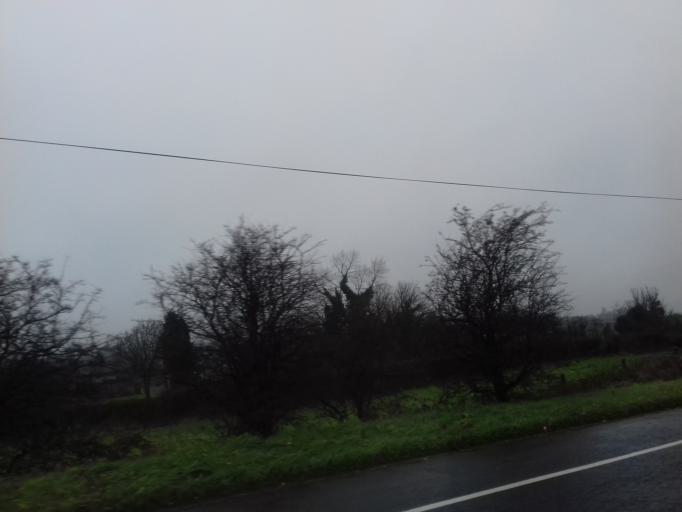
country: GB
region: Northern Ireland
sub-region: Strabane District
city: Sion Mills
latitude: 54.7471
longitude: -7.4434
